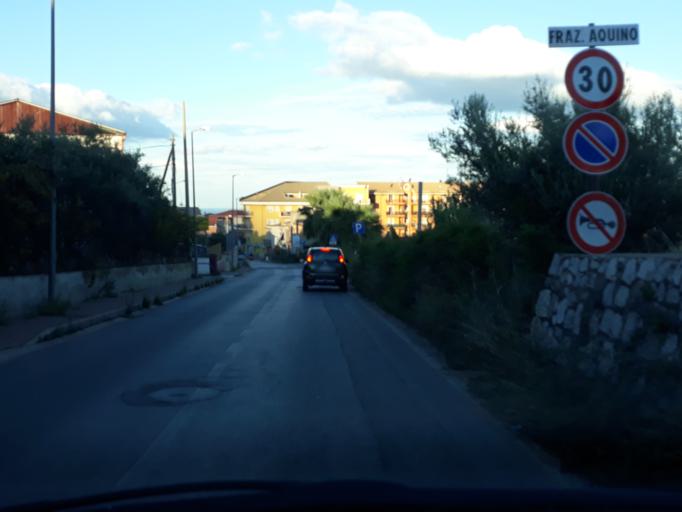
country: IT
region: Sicily
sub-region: Palermo
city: Monreale
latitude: 38.0729
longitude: 13.3006
